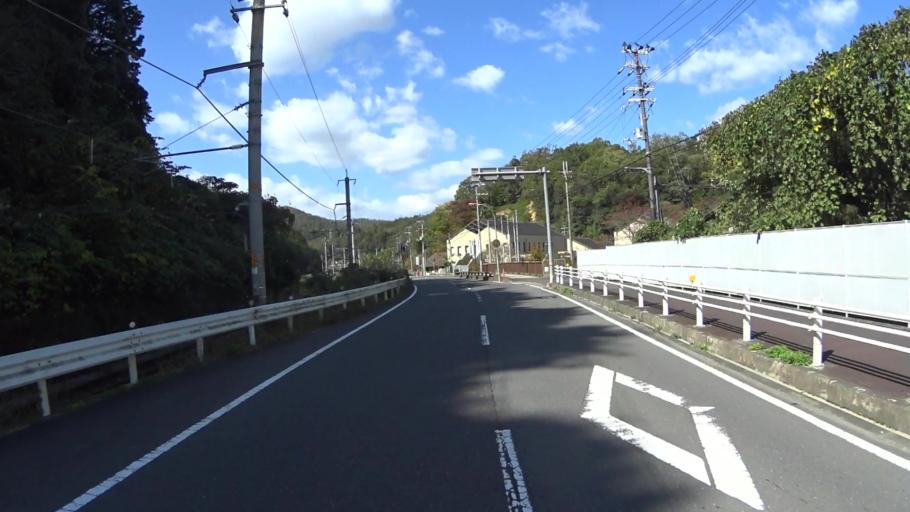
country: JP
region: Kyoto
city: Kameoka
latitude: 35.1641
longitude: 135.5016
